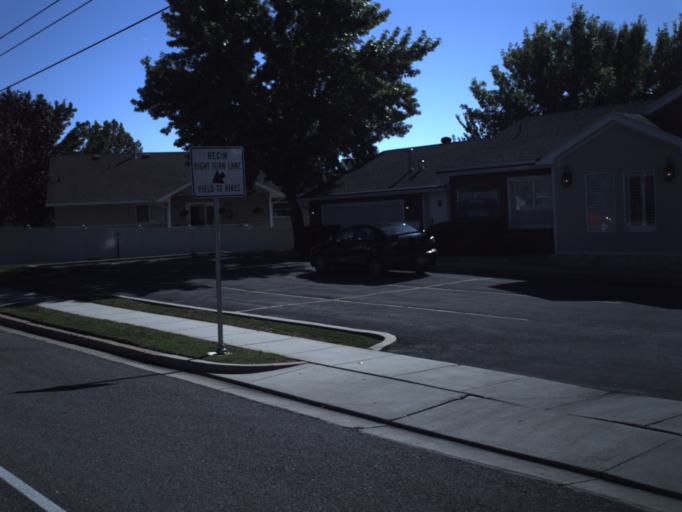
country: US
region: Utah
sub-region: Davis County
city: Kaysville
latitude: 41.0315
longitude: -111.9365
